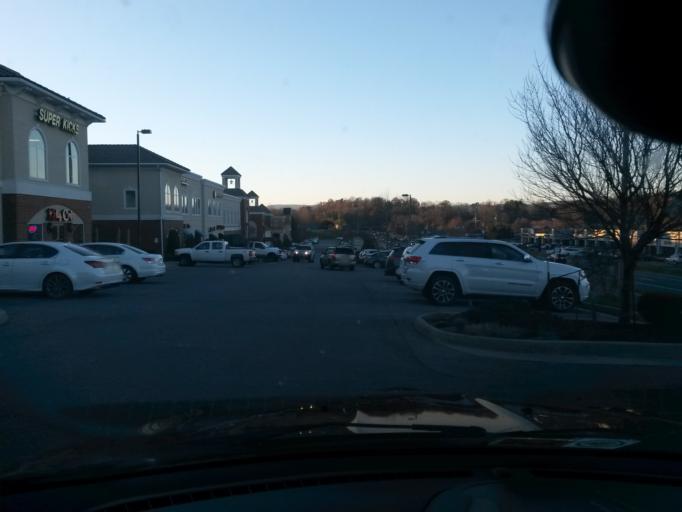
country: US
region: Virginia
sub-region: Roanoke County
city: Cave Spring
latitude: 37.2252
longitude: -79.9971
